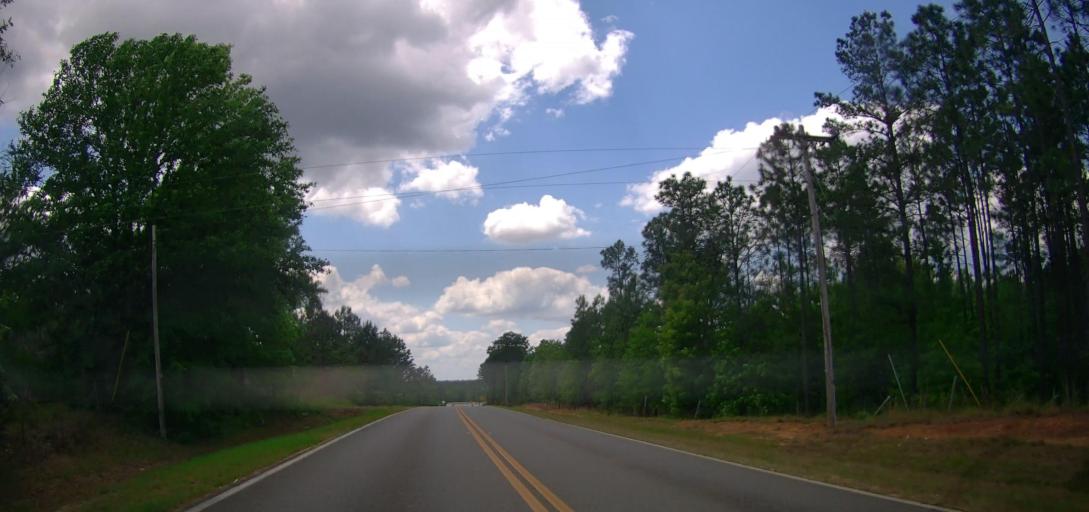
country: US
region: Georgia
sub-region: Laurens County
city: East Dublin
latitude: 32.5232
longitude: -82.7620
